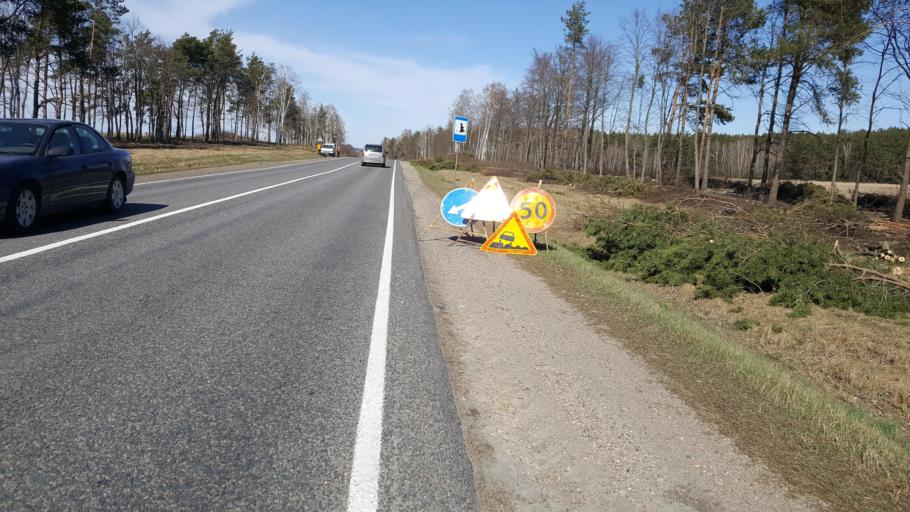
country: BY
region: Brest
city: Charnawchytsy
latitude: 52.2908
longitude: 23.7755
